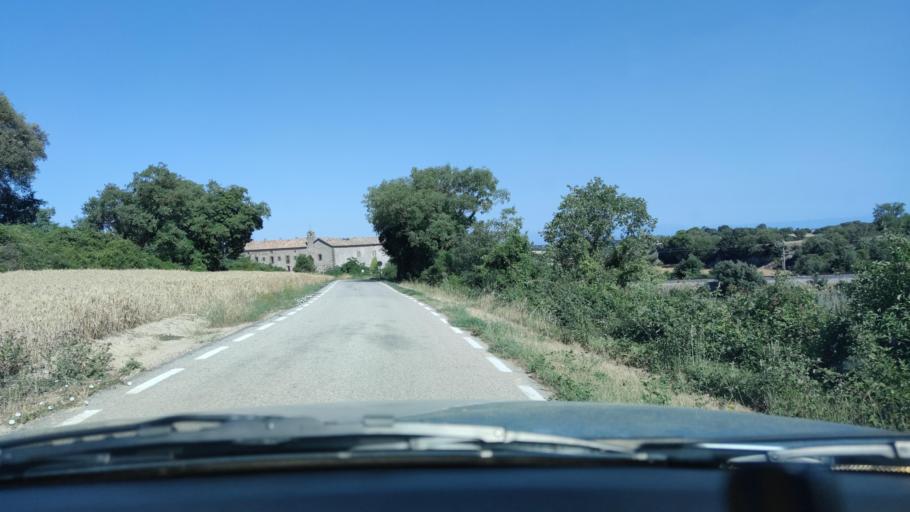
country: ES
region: Catalonia
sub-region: Provincia de Lleida
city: Sant Guim de Freixenet
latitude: 41.6480
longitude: 1.4089
